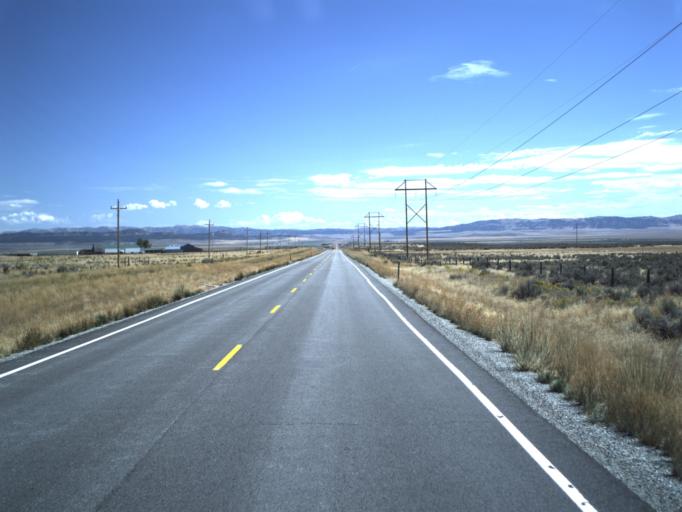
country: US
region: Idaho
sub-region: Oneida County
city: Malad City
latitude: 41.9657
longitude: -113.0046
